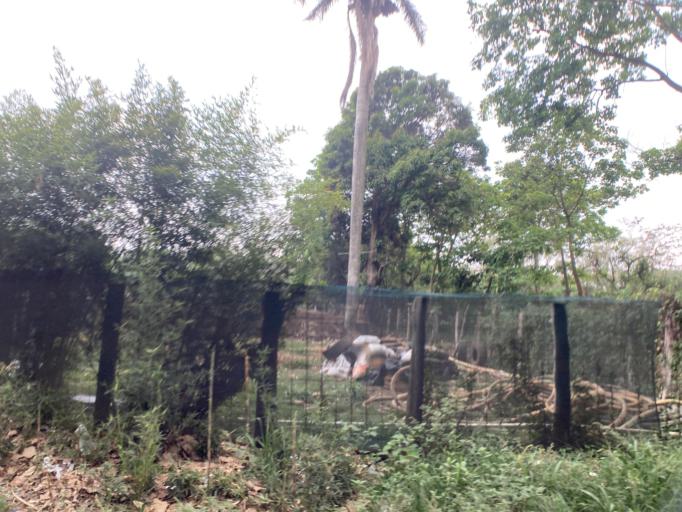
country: GT
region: Guatemala
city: Fraijanes
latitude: 14.3970
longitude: -90.4752
